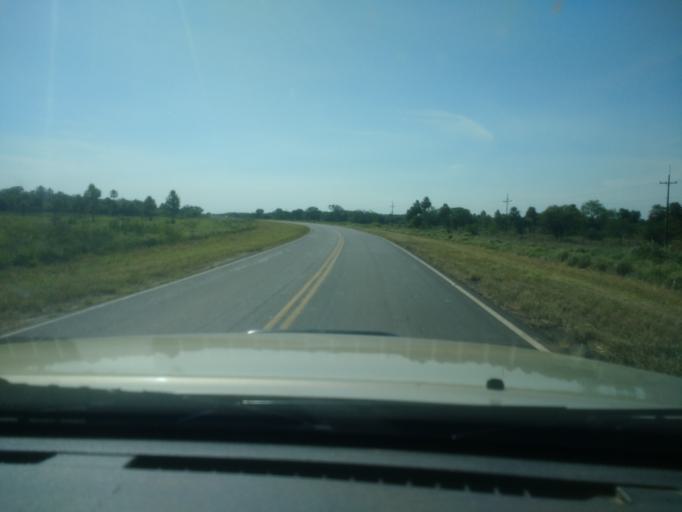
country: PY
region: Presidente Hayes
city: Benjamin Aceval
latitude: -24.9075
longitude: -57.6447
